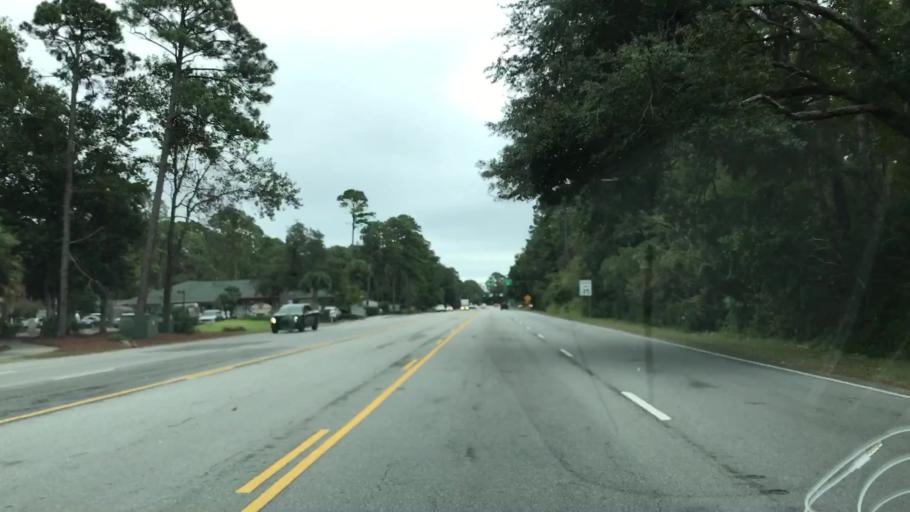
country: US
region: South Carolina
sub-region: Beaufort County
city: Hilton Head Island
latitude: 32.1606
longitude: -80.7670
